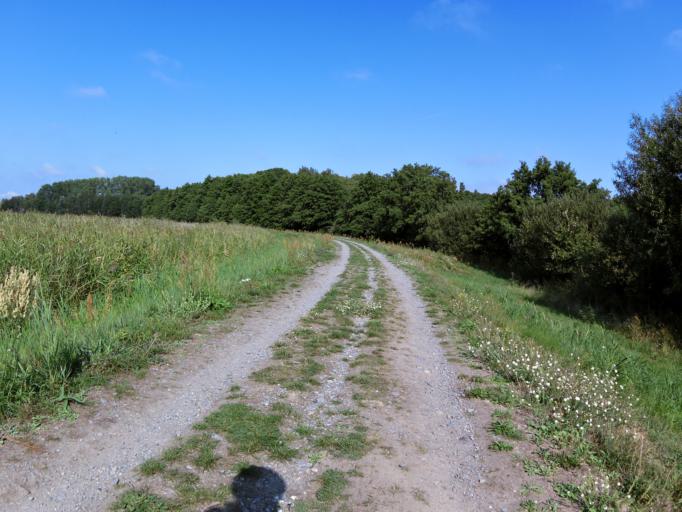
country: DE
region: Mecklenburg-Vorpommern
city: Loddin
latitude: 53.9975
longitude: 14.0487
